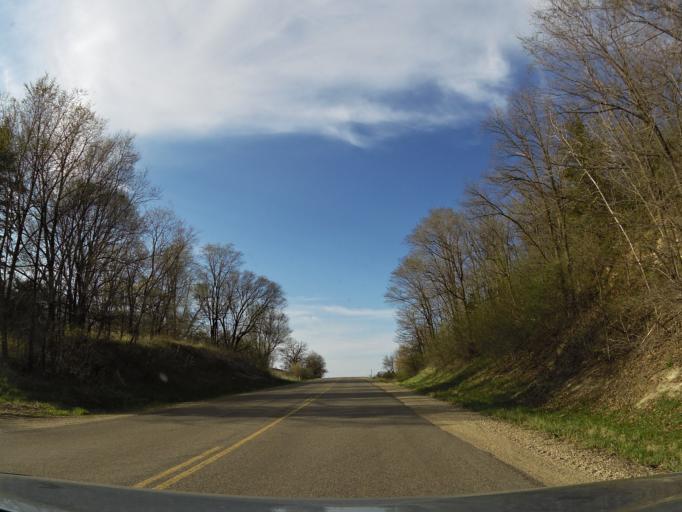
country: US
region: Wisconsin
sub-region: Pierce County
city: River Falls
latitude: 44.7554
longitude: -92.6395
